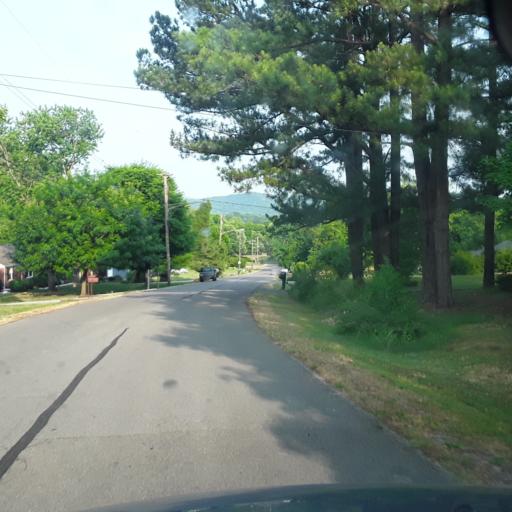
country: US
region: Tennessee
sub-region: Davidson County
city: Oak Hill
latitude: 36.0618
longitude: -86.7246
